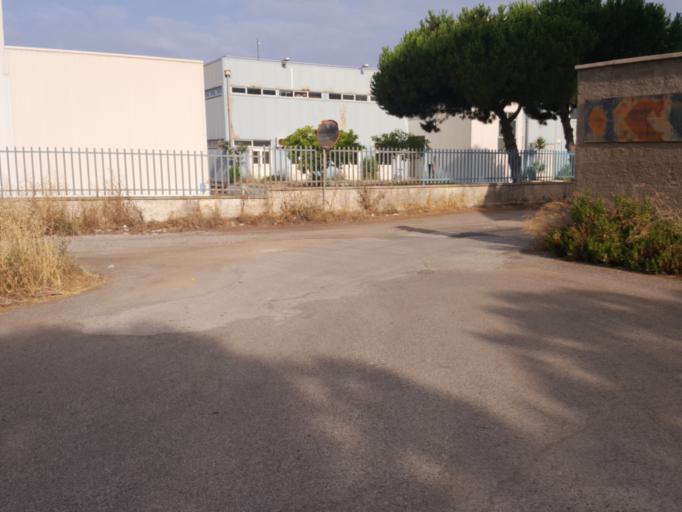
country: IT
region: Latium
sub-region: Citta metropolitana di Roma Capitale
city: Civitavecchia
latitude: 42.1016
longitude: 11.7890
